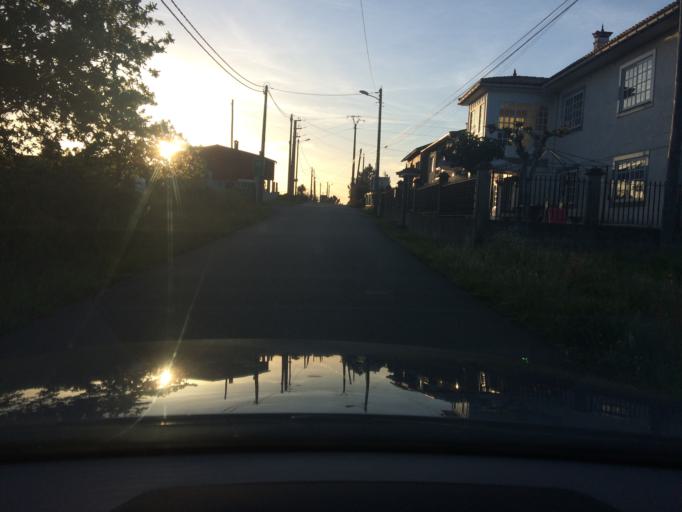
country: ES
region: Galicia
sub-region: Provincia da Coruna
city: Santiago de Compostela
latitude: 42.8335
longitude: -8.6012
